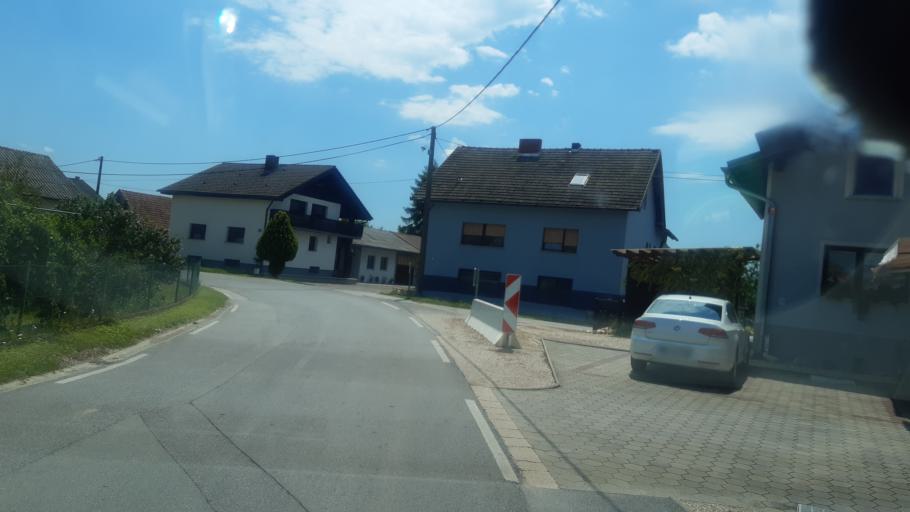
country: SI
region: Beltinci
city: Gancani
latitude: 46.6576
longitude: 16.2582
